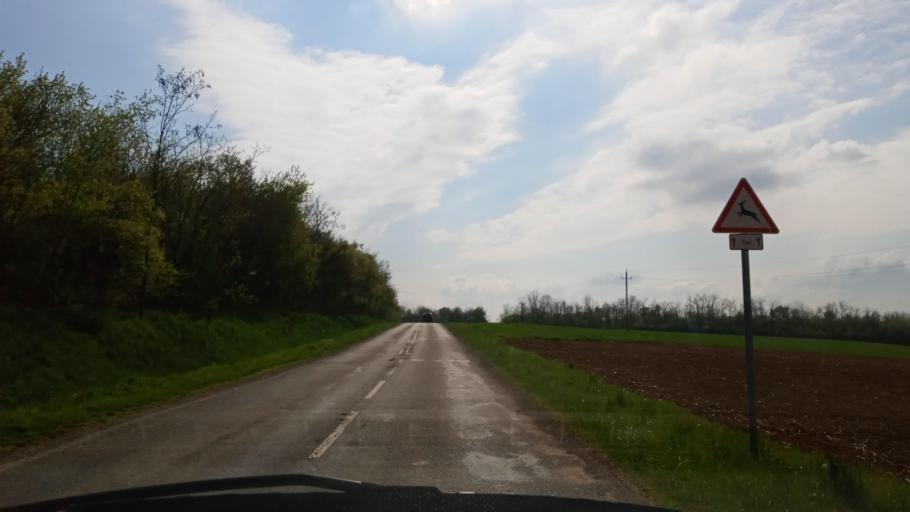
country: HU
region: Baranya
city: Pecsvarad
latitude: 46.1523
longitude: 18.4445
